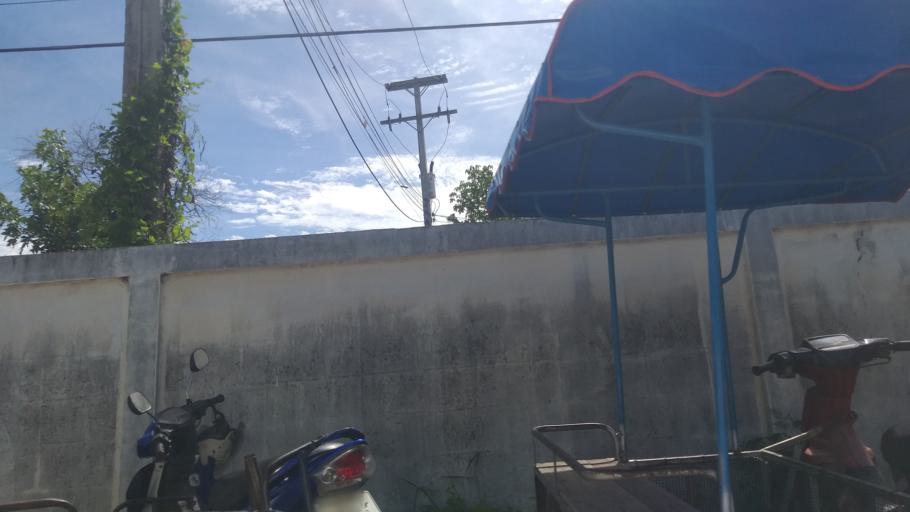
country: TH
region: Chaiyaphum
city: Ban Thaen
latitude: 16.4064
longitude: 102.3443
